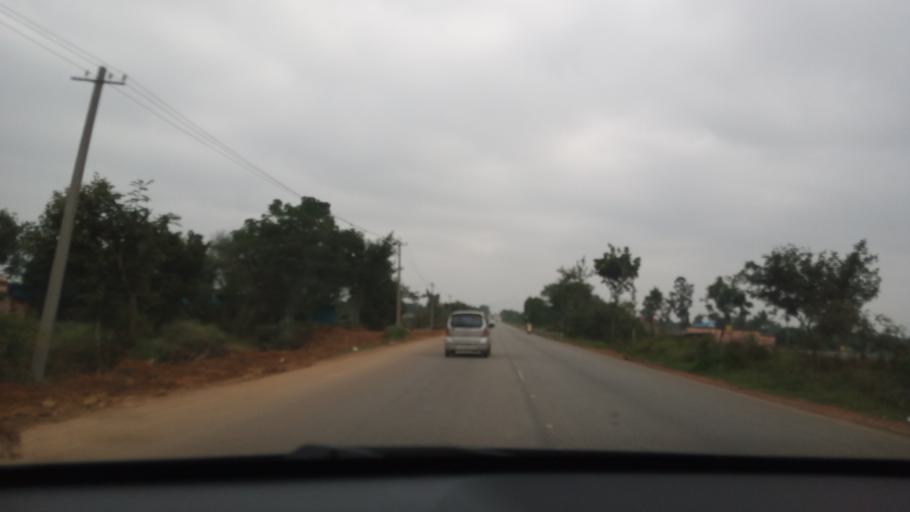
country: IN
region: Karnataka
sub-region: Bangalore Rural
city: Vijayapura
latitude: 13.2645
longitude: 77.9457
